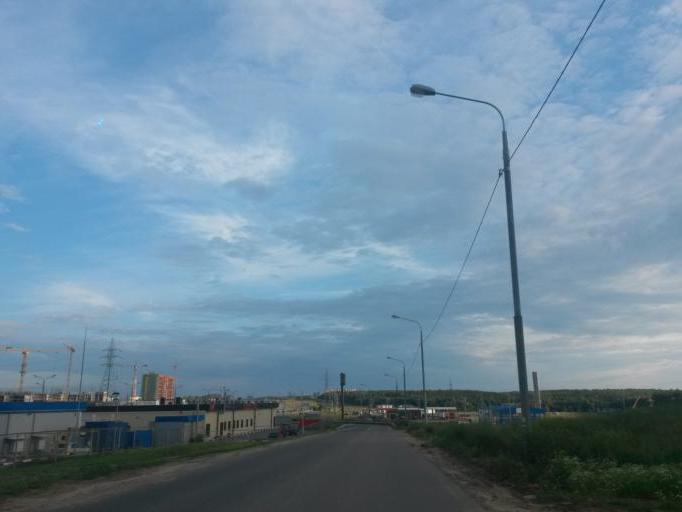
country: RU
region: Moskovskaya
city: Vostryakovo
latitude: 55.3948
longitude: 37.7758
